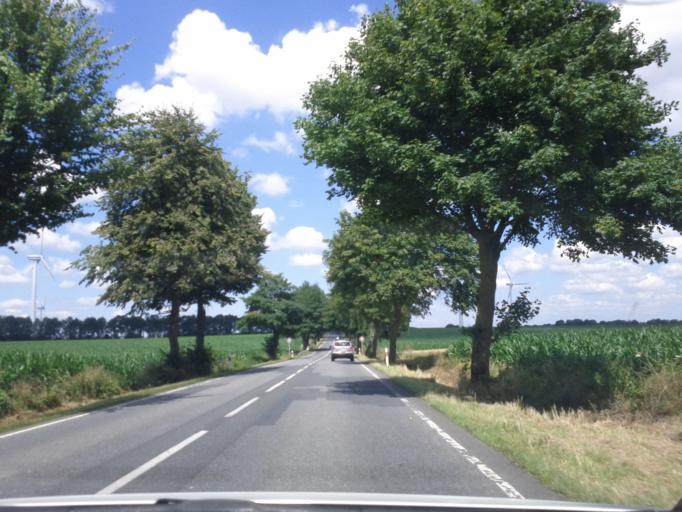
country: DE
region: Lower Saxony
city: Apensen
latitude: 53.4520
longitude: 9.6048
